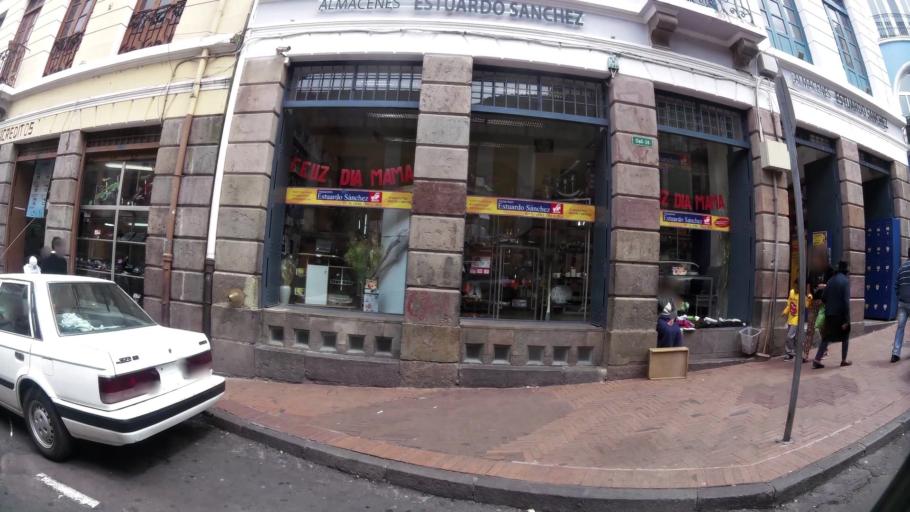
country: EC
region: Pichincha
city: Quito
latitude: -0.2218
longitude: -78.5145
